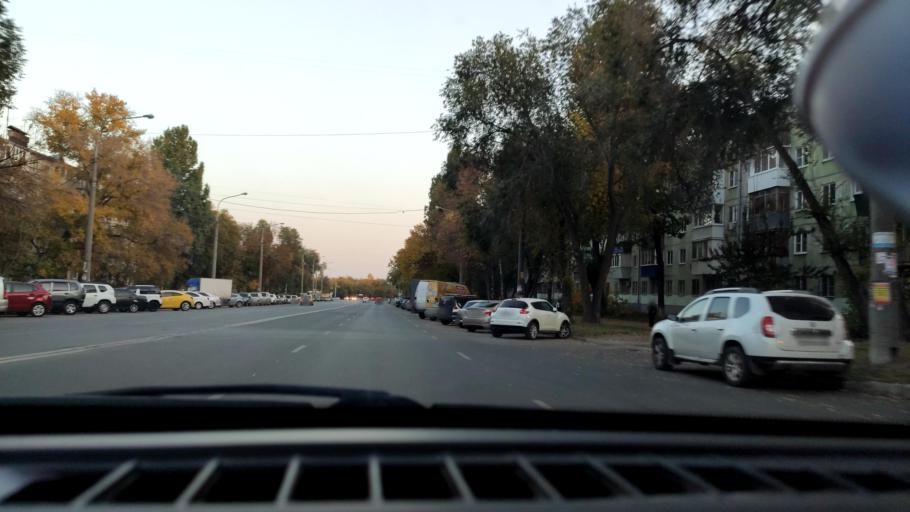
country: RU
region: Samara
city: Samara
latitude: 53.2279
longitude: 50.2080
